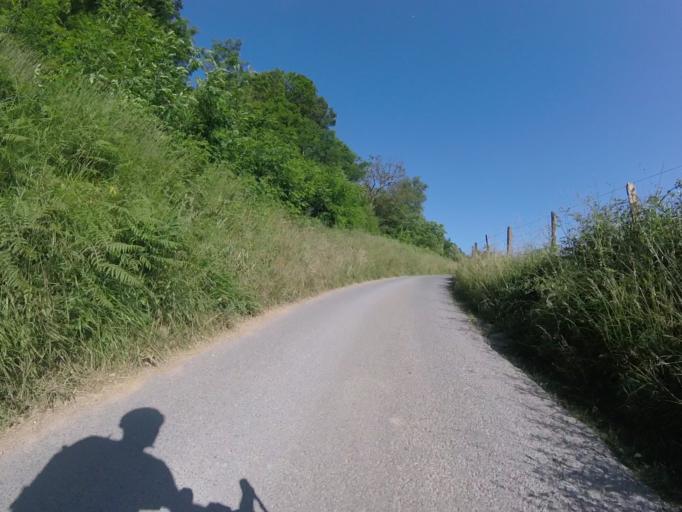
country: ES
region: Basque Country
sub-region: Provincia de Guipuzcoa
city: Astigarraga
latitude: 43.2922
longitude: -1.9356
